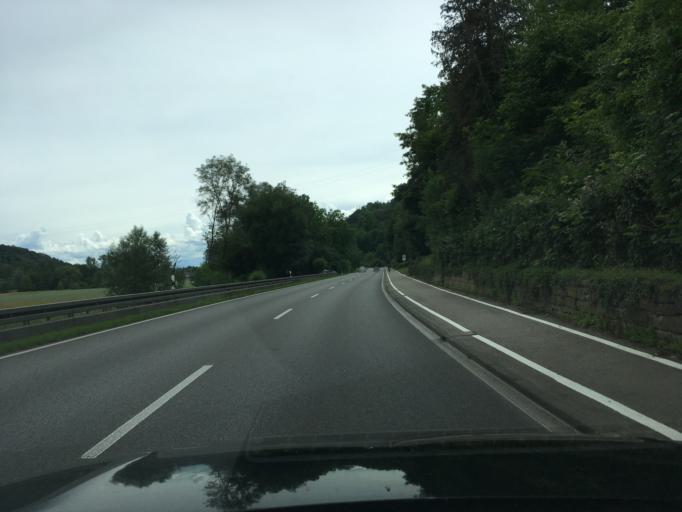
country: DE
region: Baden-Wuerttemberg
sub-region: Regierungsbezirk Stuttgart
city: Besigheim
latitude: 48.9834
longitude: 9.1475
